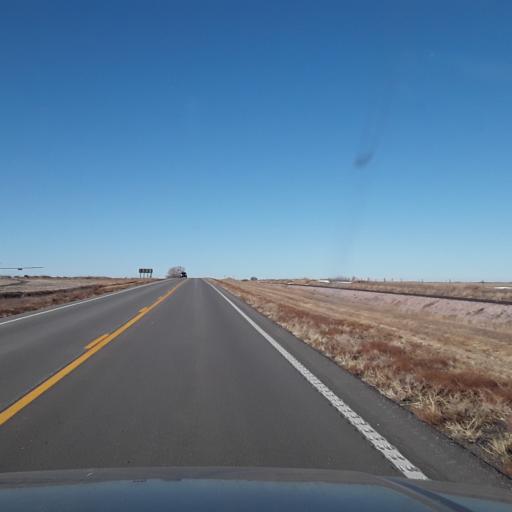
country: US
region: Nebraska
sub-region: Phelps County
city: Holdrege
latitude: 40.4834
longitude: -99.5186
